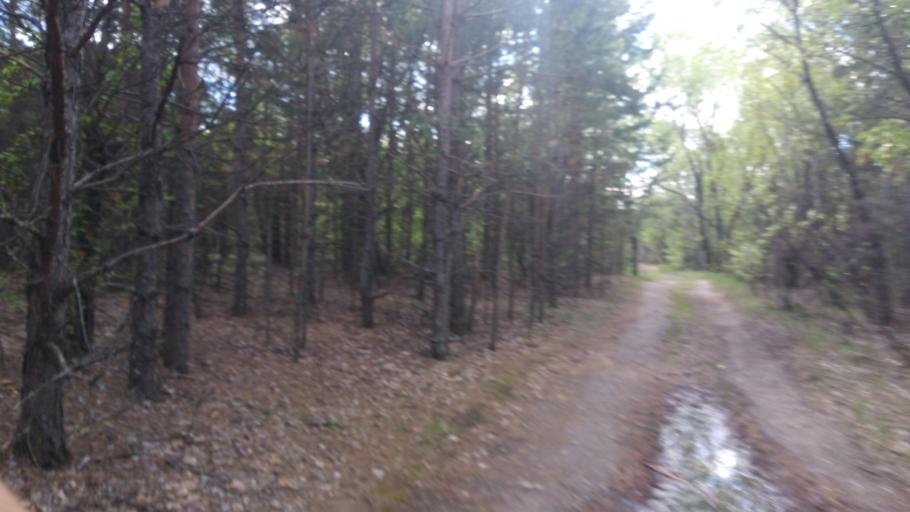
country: RU
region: Chelyabinsk
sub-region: Gorod Chelyabinsk
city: Chelyabinsk
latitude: 55.1691
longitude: 61.3398
